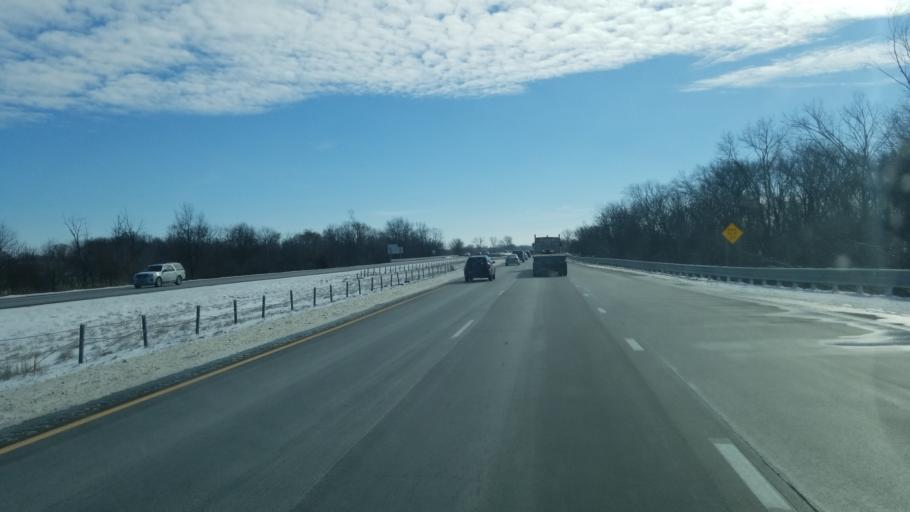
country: US
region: Michigan
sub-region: Washtenaw County
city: Milan
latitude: 42.0280
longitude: -83.6790
